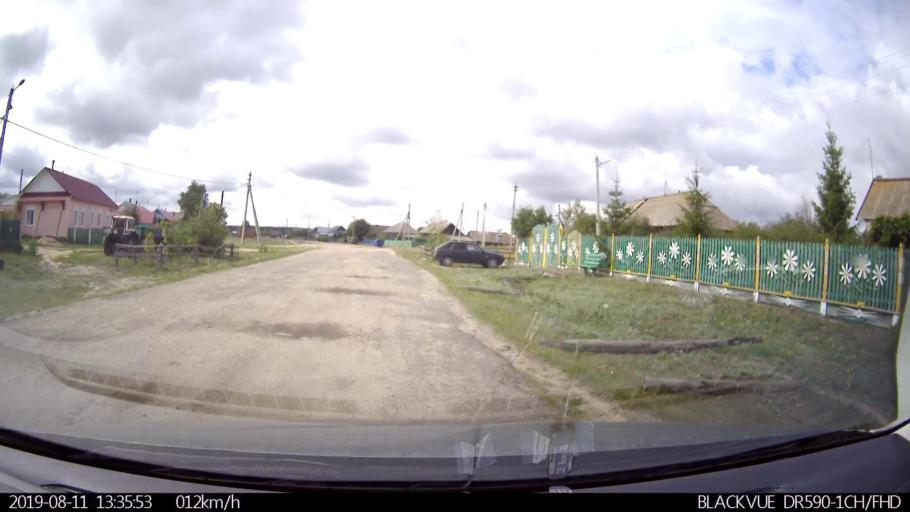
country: RU
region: Ulyanovsk
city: Ignatovka
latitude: 53.8598
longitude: 47.5877
